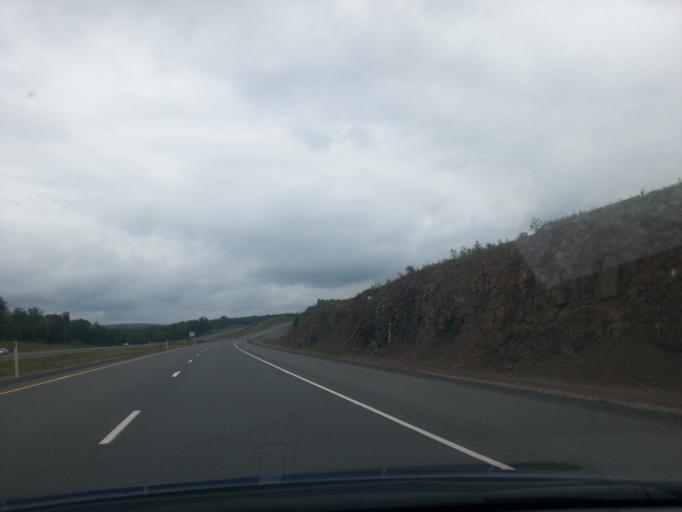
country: US
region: Maine
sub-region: Aroostook County
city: Limestone
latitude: 46.8668
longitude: -67.7193
